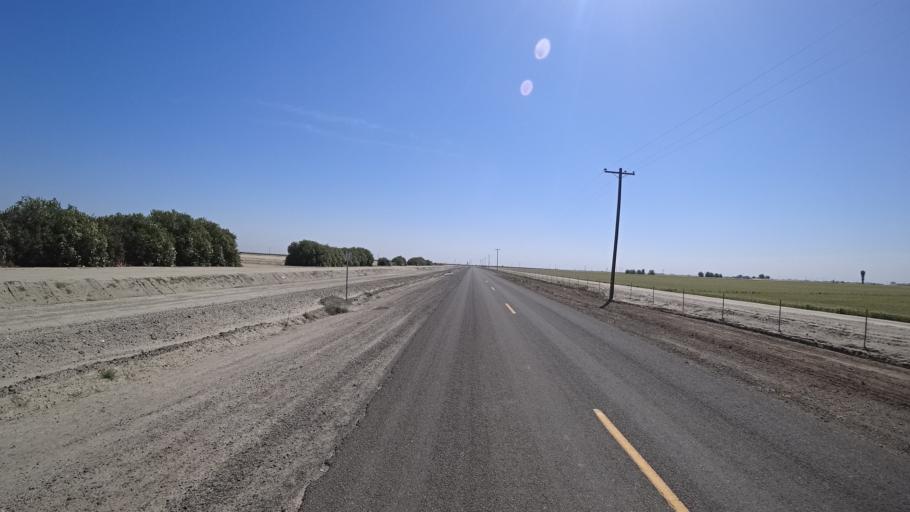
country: US
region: California
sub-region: Kings County
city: Corcoran
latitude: 36.0726
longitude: -119.5448
